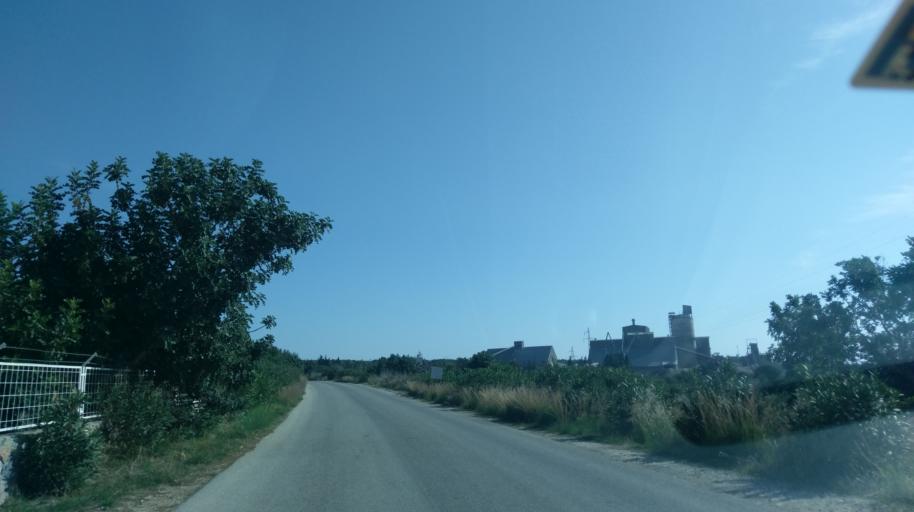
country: CY
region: Ammochostos
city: Trikomo
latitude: 35.3270
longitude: 34.0026
